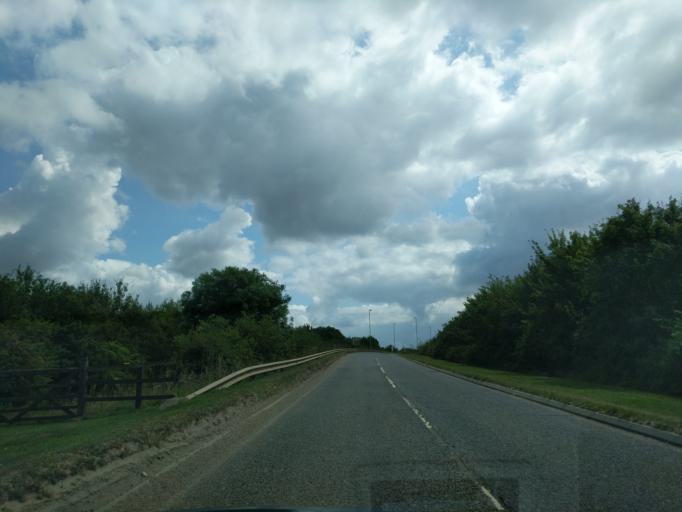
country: GB
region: England
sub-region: Cambridgeshire
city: Isleham
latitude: 52.2900
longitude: 0.4670
